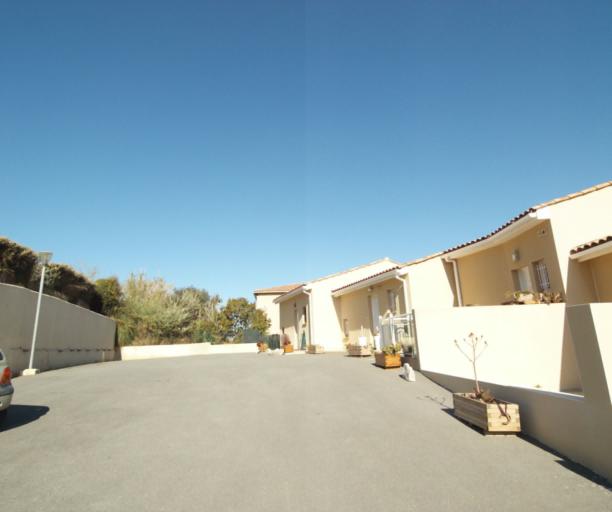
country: FR
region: Corsica
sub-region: Departement de la Corse-du-Sud
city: Propriano
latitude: 41.6715
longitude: 8.9002
